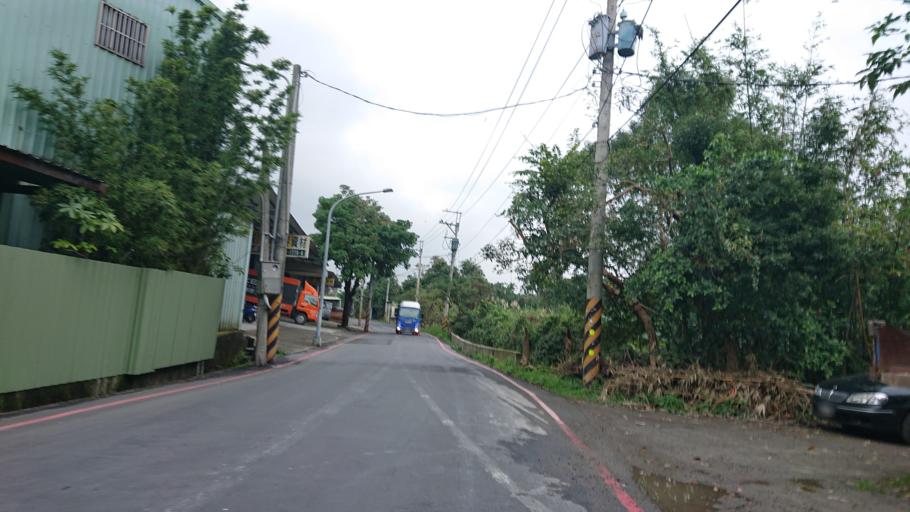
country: TW
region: Taiwan
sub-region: Taoyuan
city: Taoyuan
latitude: 24.9490
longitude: 121.3892
